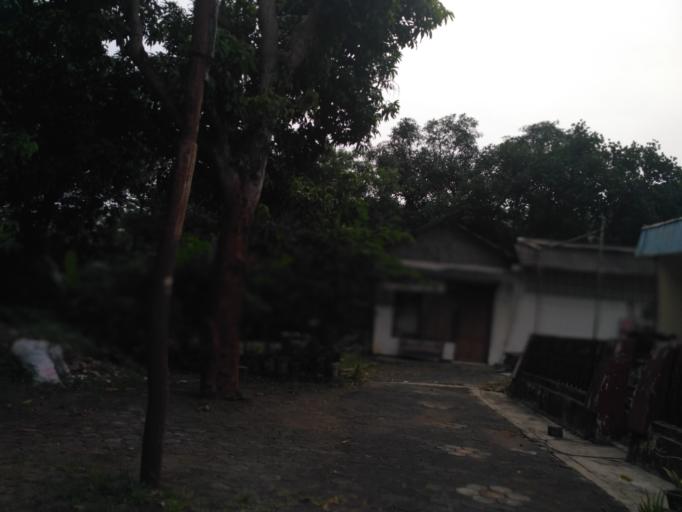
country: ID
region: Central Java
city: Ungaran
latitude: -7.0740
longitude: 110.4280
